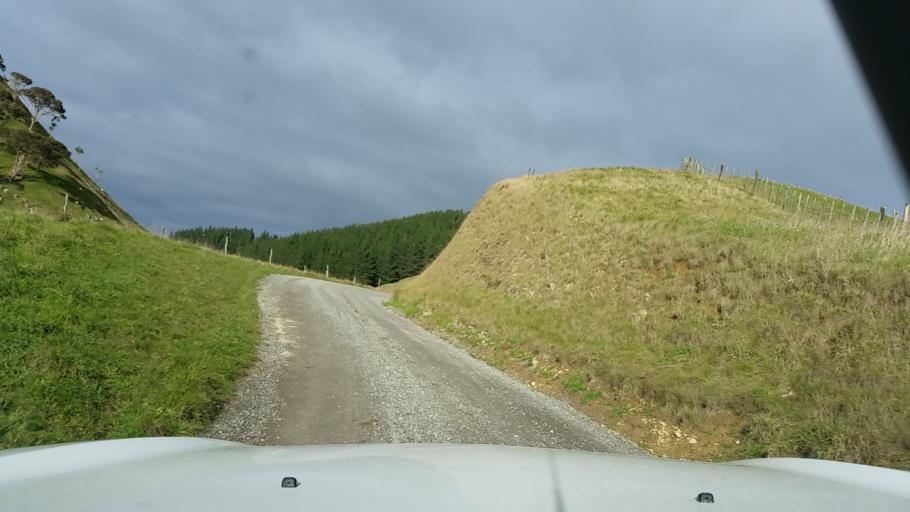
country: NZ
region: Wellington
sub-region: Masterton District
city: Masterton
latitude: -41.0359
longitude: 175.7130
